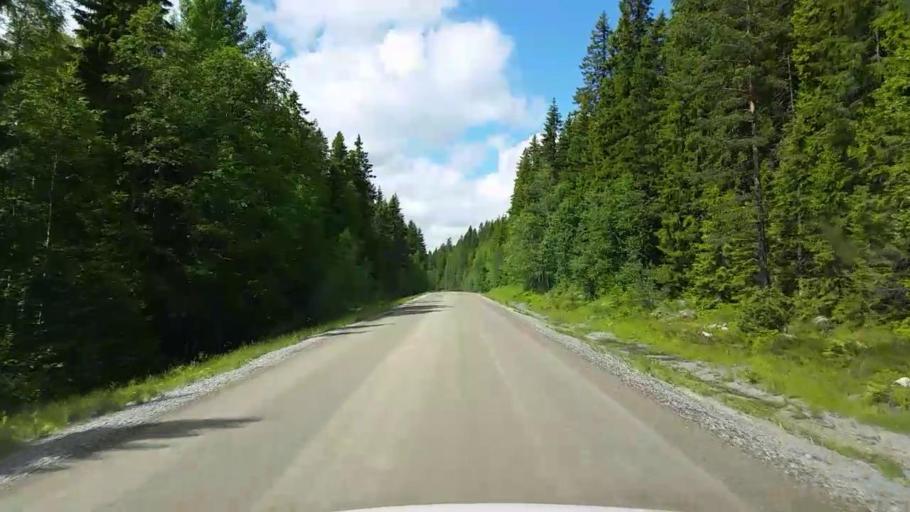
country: SE
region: Gaevleborg
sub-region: Bollnas Kommun
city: Vittsjo
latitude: 61.0417
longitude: 16.3490
